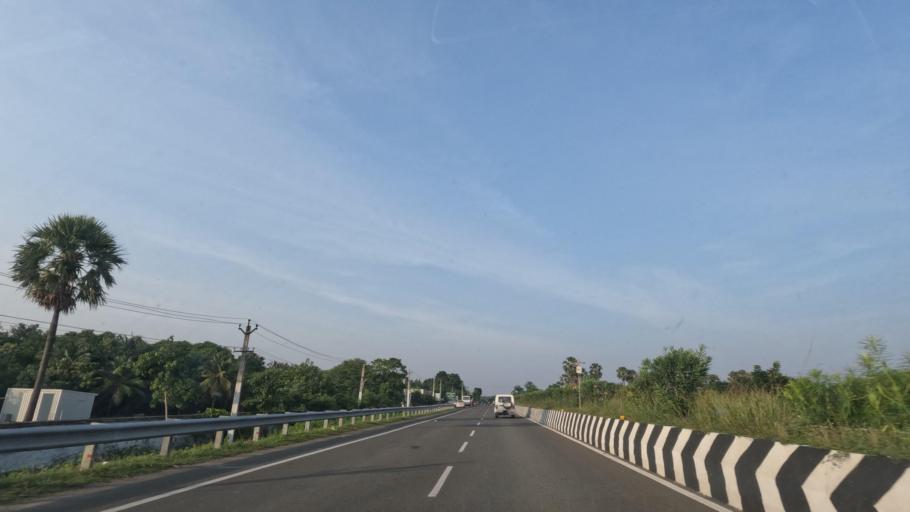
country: IN
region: Tamil Nadu
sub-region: Kancheepuram
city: Mamallapuram
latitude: 12.6553
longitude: 80.2070
